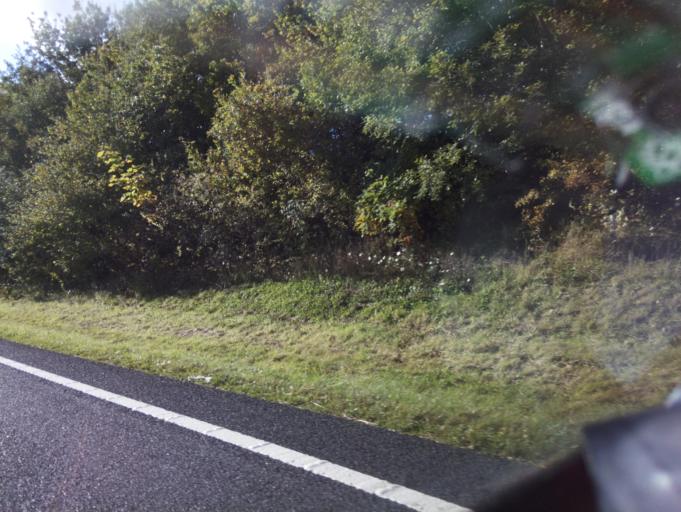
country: GB
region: Wales
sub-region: Sir Powys
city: Brecon
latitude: 51.9687
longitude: -3.3449
